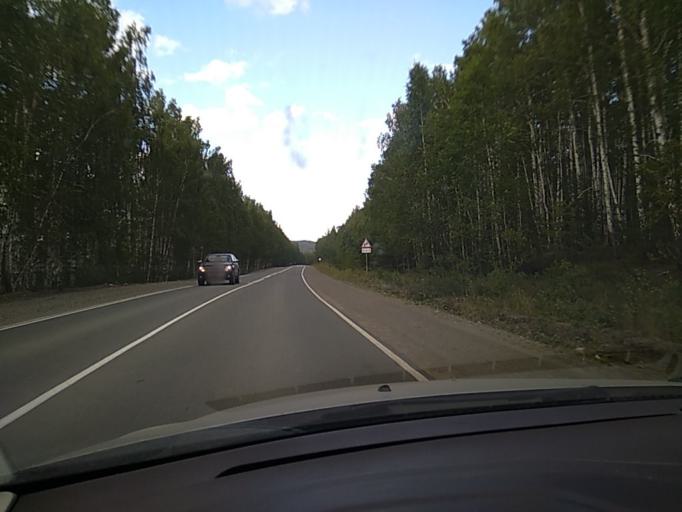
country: RU
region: Chelyabinsk
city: Karabash
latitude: 55.5002
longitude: 60.2587
